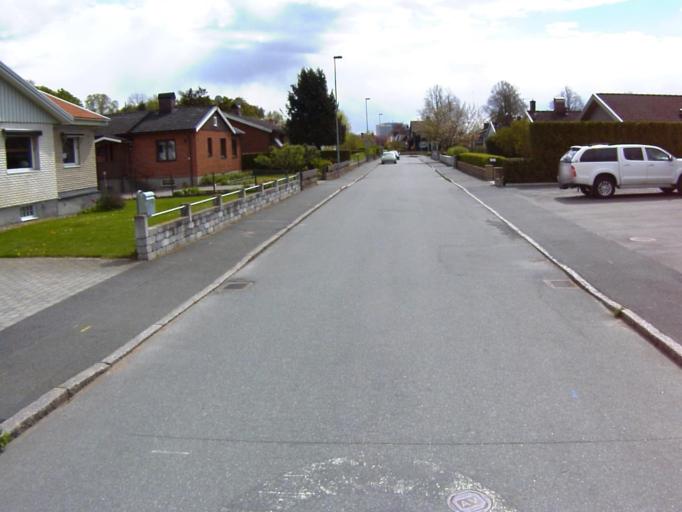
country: SE
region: Skane
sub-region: Kristianstads Kommun
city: Kristianstad
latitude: 56.0412
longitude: 14.1708
